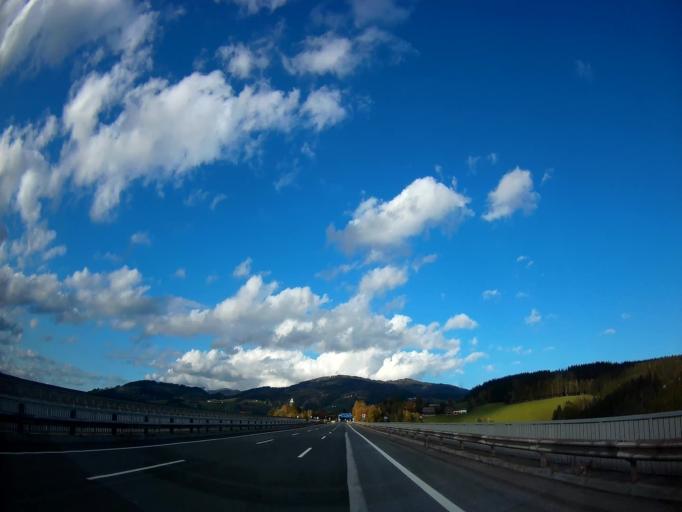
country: AT
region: Carinthia
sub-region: Politischer Bezirk Wolfsberg
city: Bad Sankt Leonhard im Lavanttal
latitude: 46.9235
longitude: 14.8409
